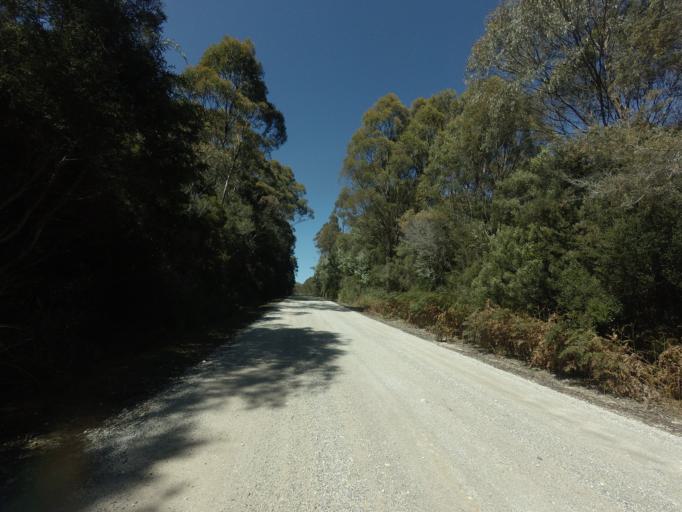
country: AU
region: Tasmania
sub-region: Huon Valley
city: Geeveston
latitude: -43.0119
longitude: 146.3639
